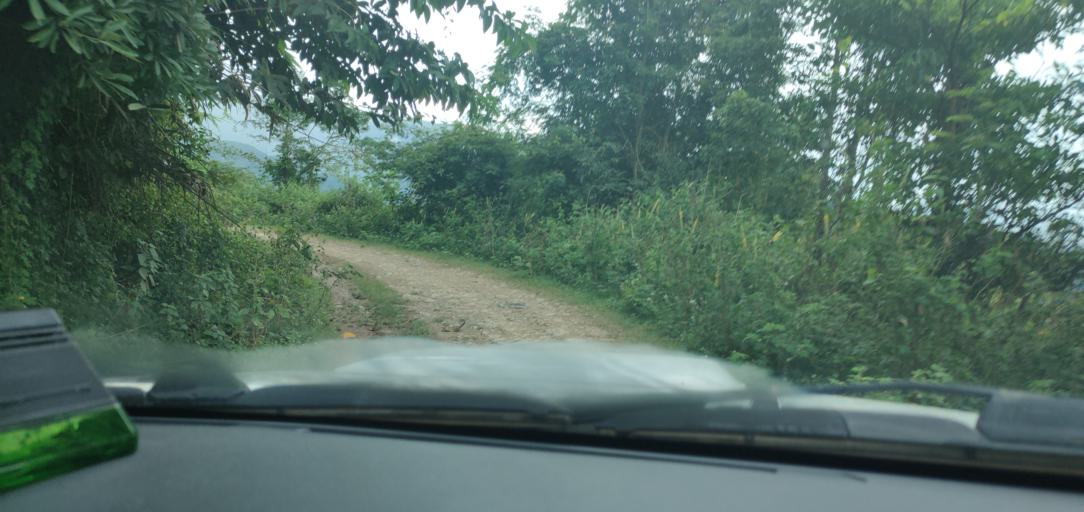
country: LA
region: Phongsali
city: Phongsali
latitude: 21.4413
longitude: 102.3232
